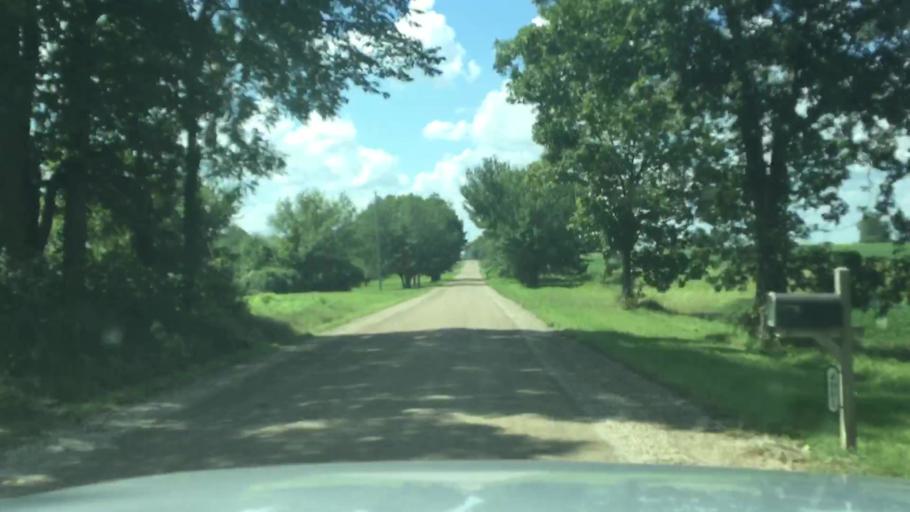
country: US
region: Michigan
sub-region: Lenawee County
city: Clinton
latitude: 42.0727
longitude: -83.9433
